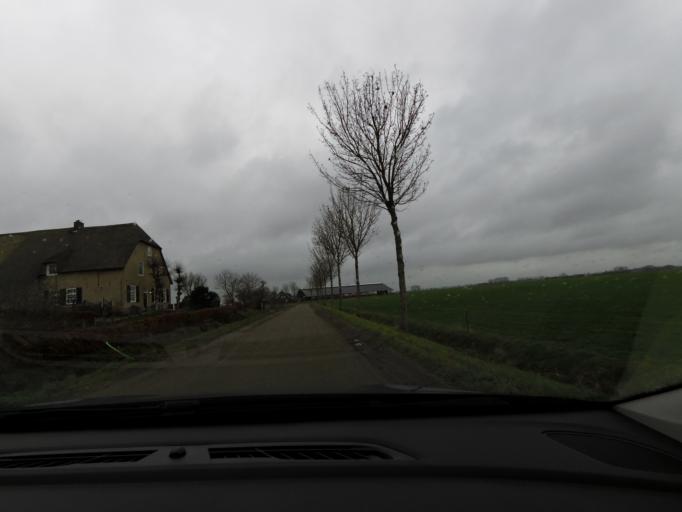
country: NL
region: North Brabant
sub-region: Gemeente Waalwijk
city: Waalwijk
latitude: 51.7482
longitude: 5.0420
